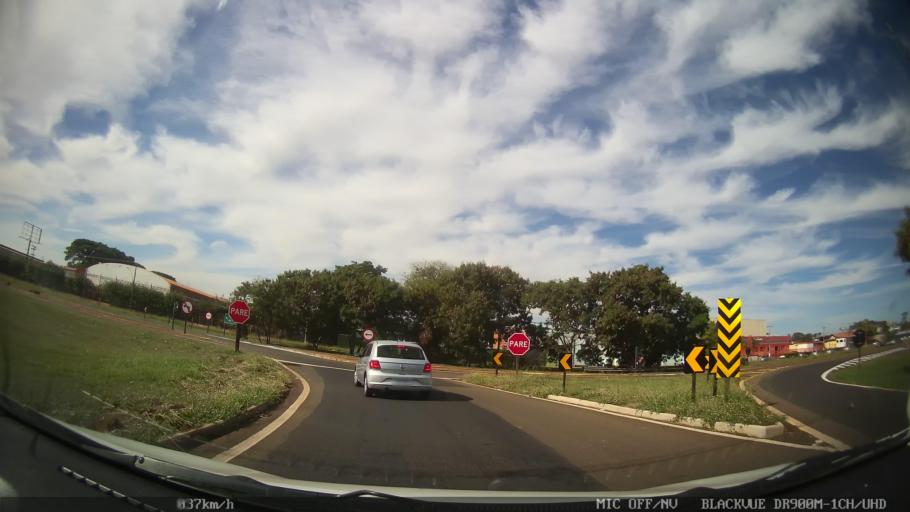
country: BR
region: Sao Paulo
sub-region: Araraquara
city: Araraquara
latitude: -21.8338
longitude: -48.1528
